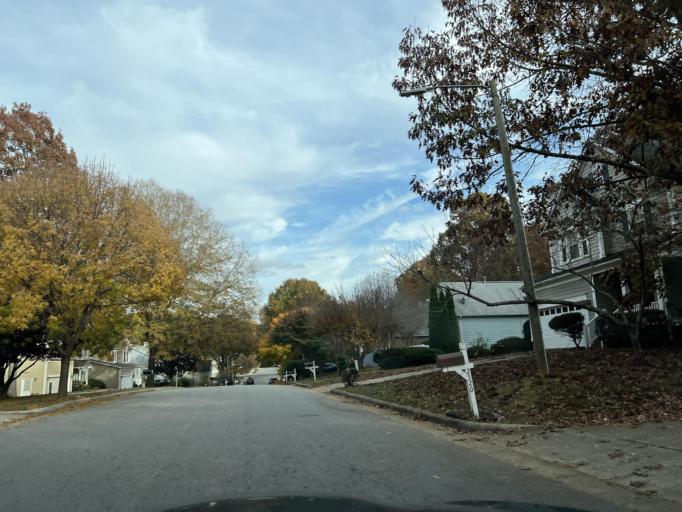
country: US
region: North Carolina
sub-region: Wake County
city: Wake Forest
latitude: 35.8997
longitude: -78.5951
